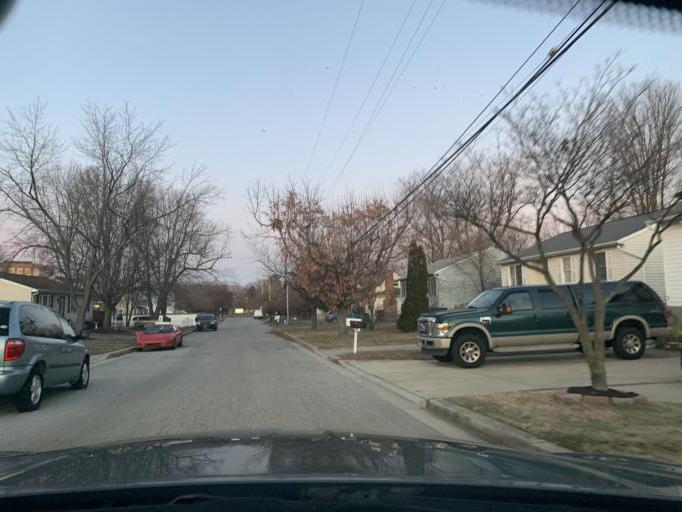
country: US
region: Maryland
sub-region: Anne Arundel County
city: Glen Burnie
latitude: 39.1479
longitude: -76.6370
